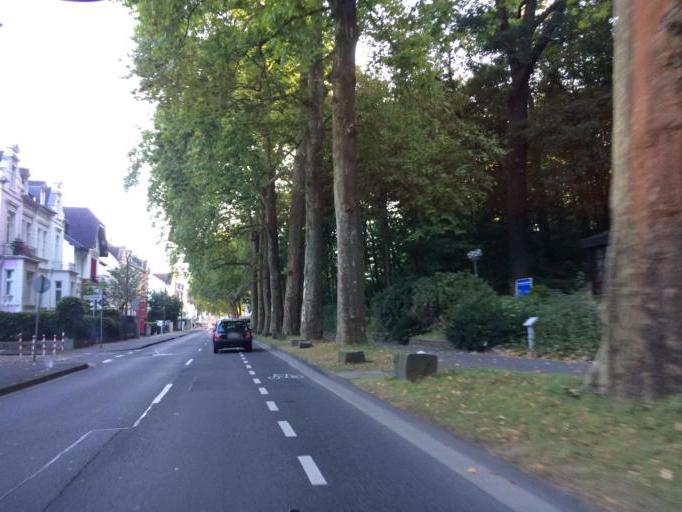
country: DE
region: North Rhine-Westphalia
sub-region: Regierungsbezirk Koln
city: Konigswinter
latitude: 50.6802
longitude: 7.1491
